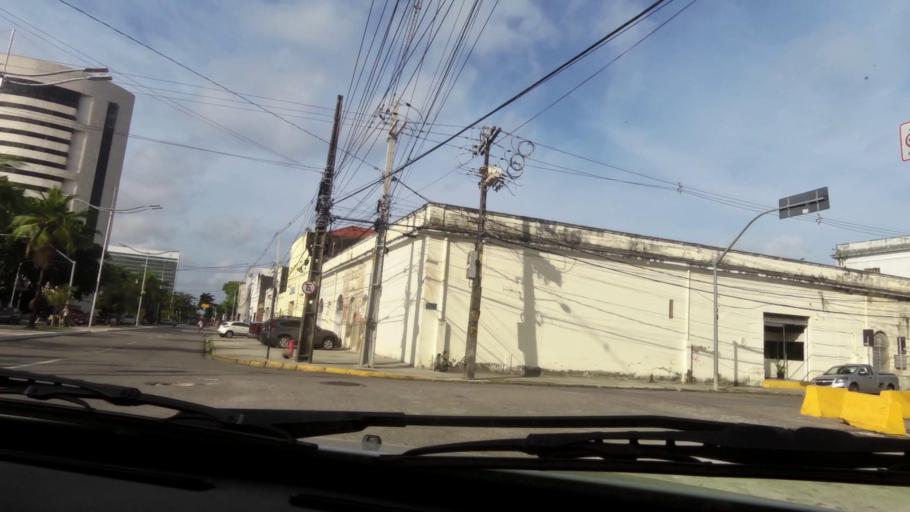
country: BR
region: Pernambuco
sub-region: Recife
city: Recife
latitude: -8.0604
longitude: -34.8726
